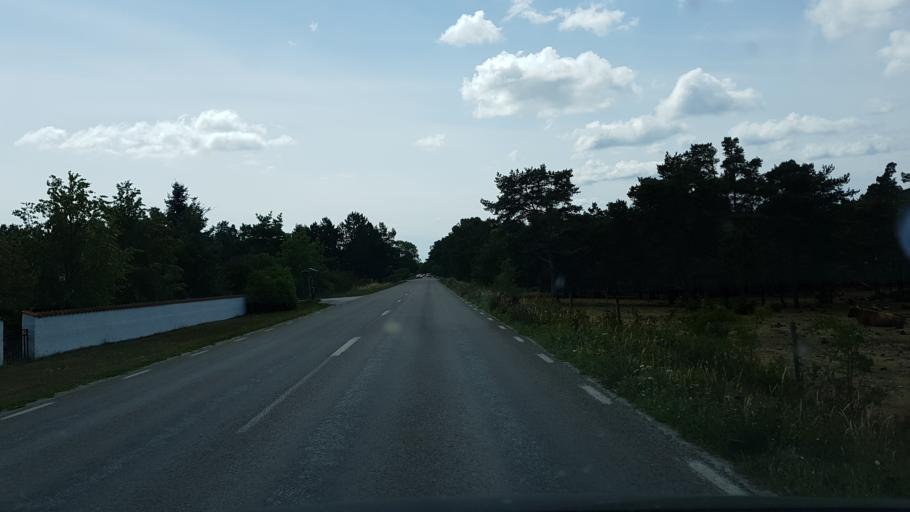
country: SE
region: Gotland
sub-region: Gotland
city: Visby
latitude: 57.7559
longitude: 18.4254
